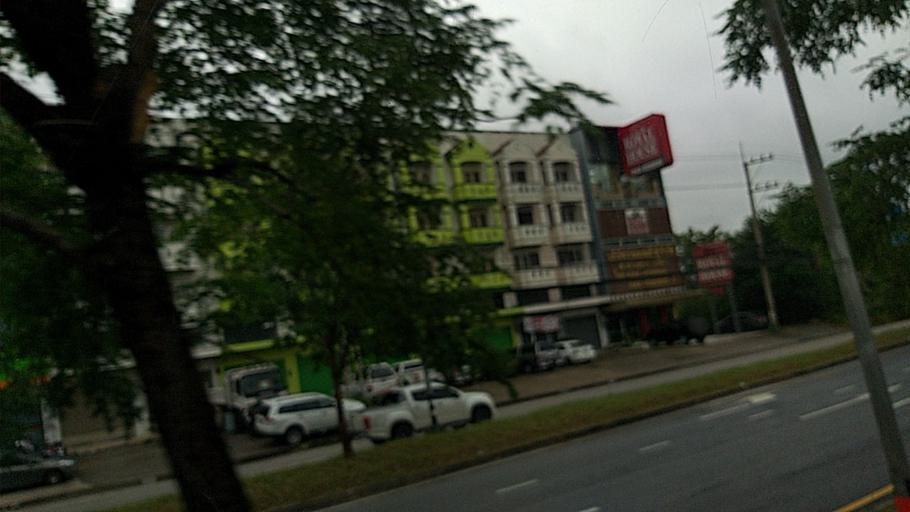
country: TH
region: Nakhon Ratchasima
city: Nakhon Ratchasima
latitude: 15.0232
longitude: 102.1353
